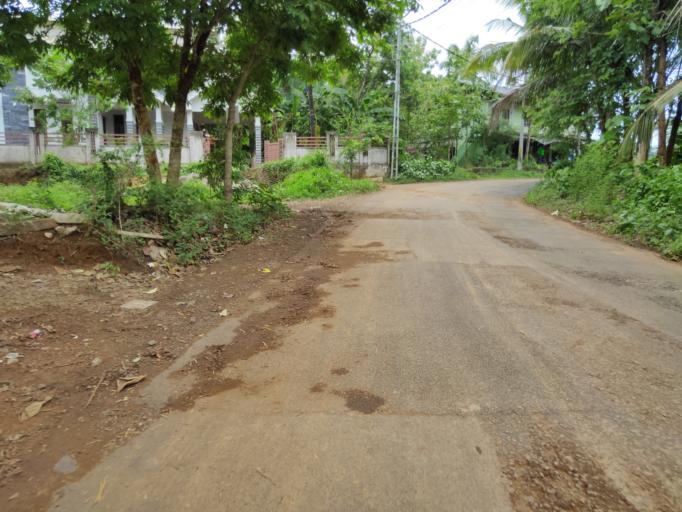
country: IN
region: Kerala
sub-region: Malappuram
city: Manjeri
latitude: 11.2472
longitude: 76.2491
